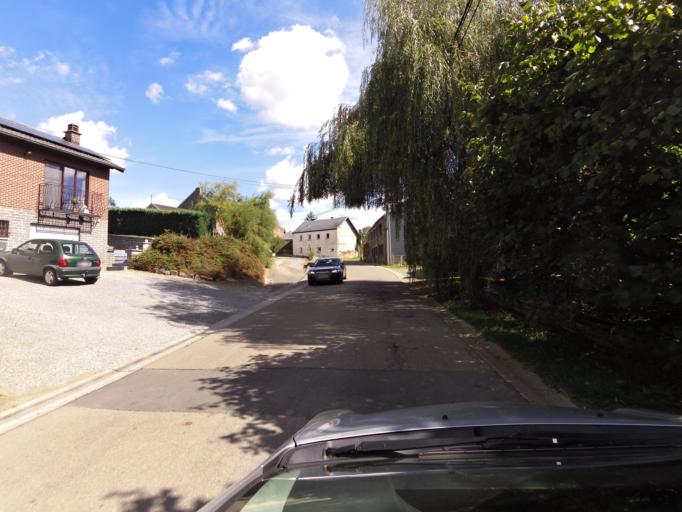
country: BE
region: Wallonia
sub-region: Province de Namur
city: Somme-Leuze
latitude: 50.3371
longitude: 5.3702
